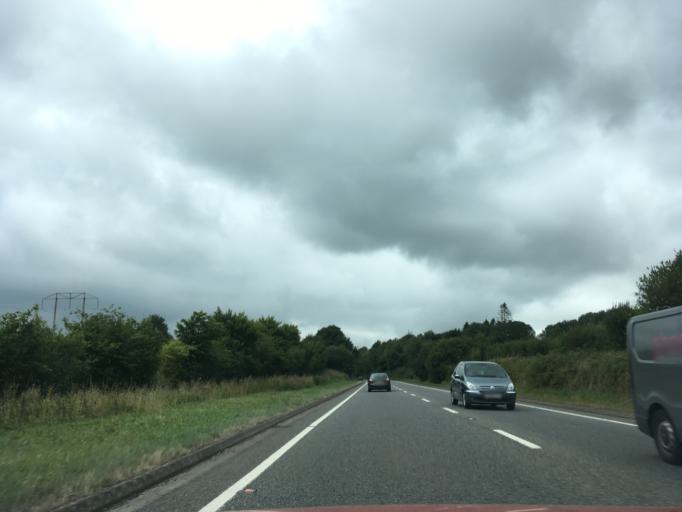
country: GB
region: Wales
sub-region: Carmarthenshire
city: Whitland
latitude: 51.8256
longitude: -4.6122
